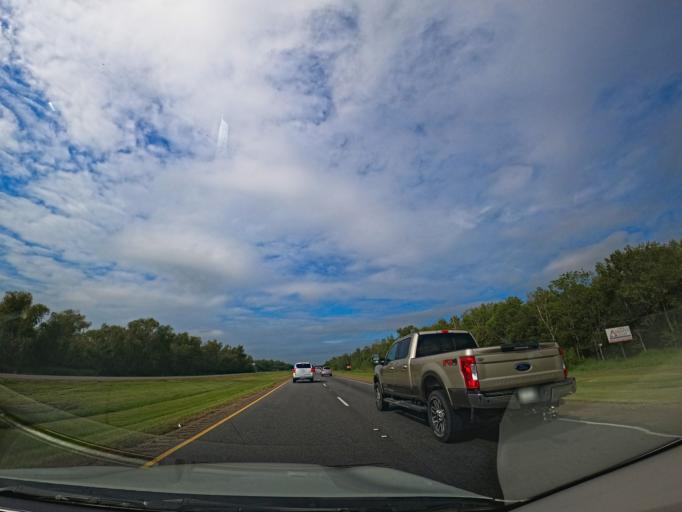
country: US
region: Louisiana
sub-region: Saint Mary Parish
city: Berwick
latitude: 29.6879
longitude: -91.2433
